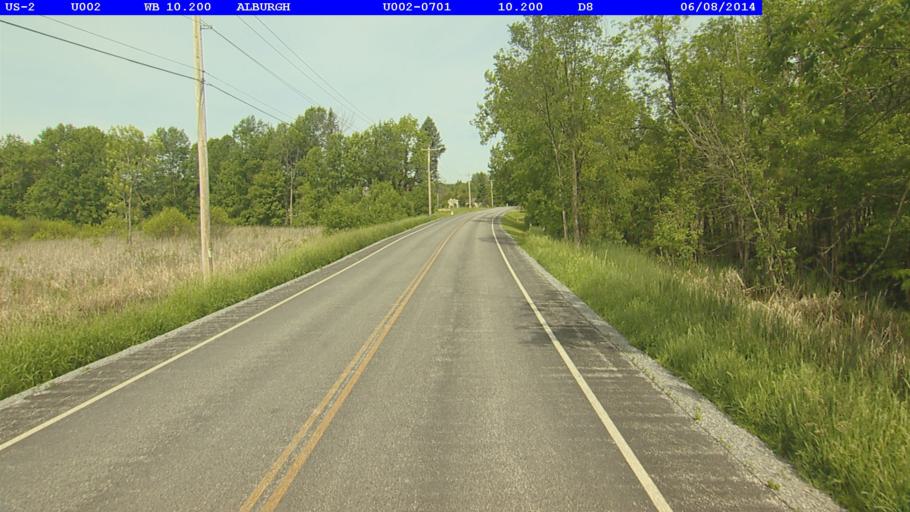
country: US
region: Vermont
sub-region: Grand Isle County
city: North Hero
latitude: 44.9052
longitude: -73.2760
